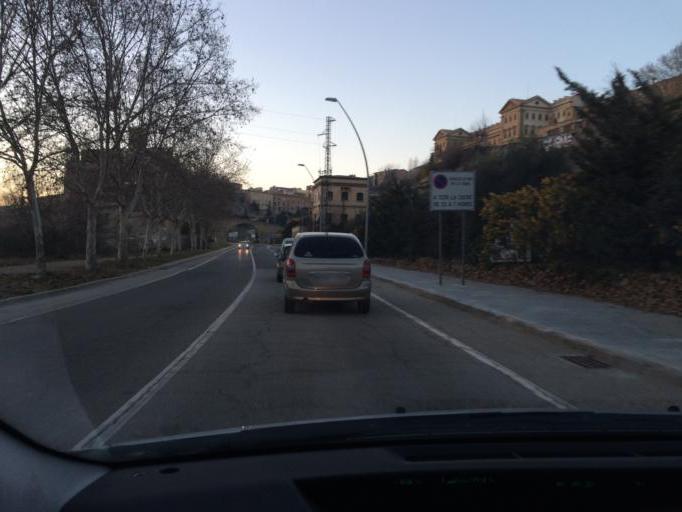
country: ES
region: Catalonia
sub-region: Provincia de Barcelona
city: Manresa
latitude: 41.7197
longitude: 1.8320
